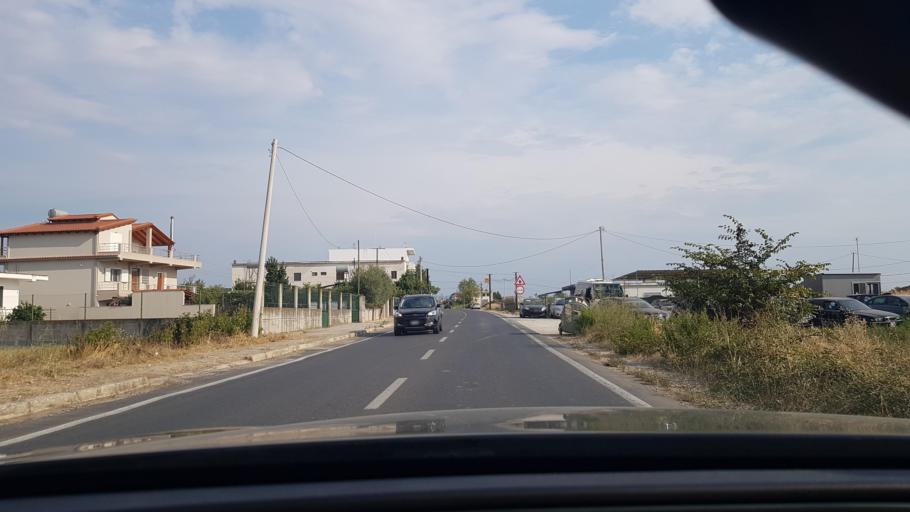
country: AL
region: Durres
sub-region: Rrethi i Durresit
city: Manze
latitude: 41.4516
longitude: 19.5697
